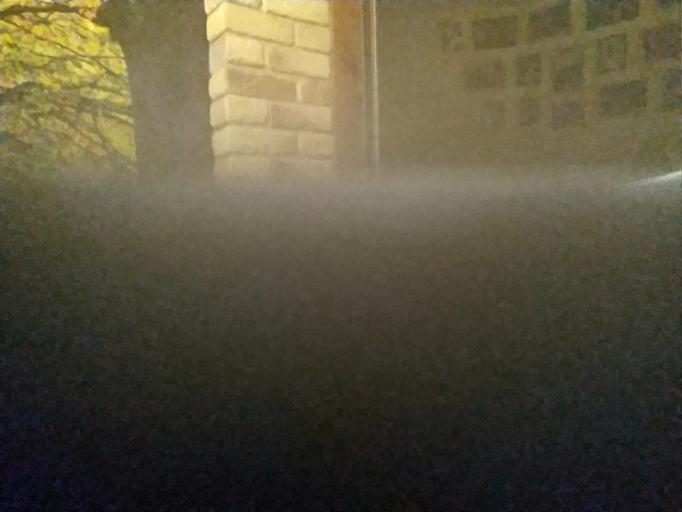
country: RU
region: Moskovskaya
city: Vysokovsk
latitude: 56.2814
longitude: 36.4599
